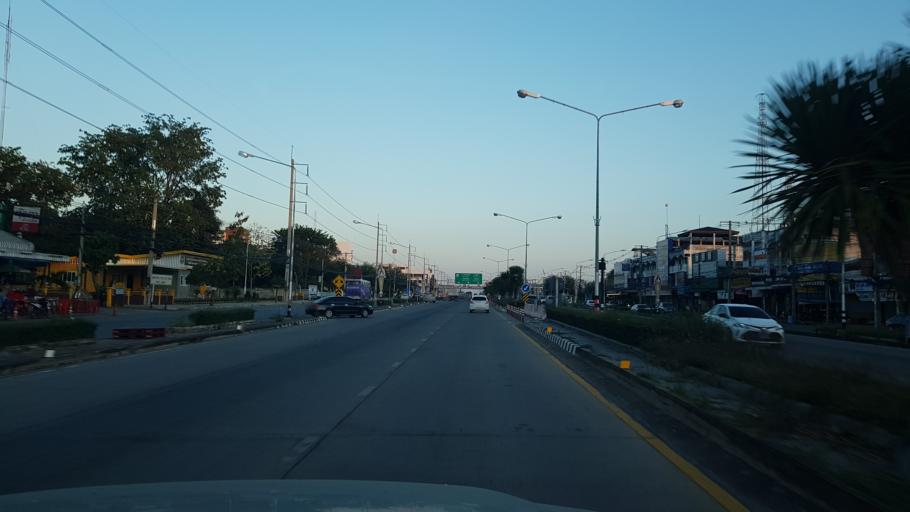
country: TH
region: Khon Kaen
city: Chum Phae
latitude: 16.5466
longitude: 102.0964
